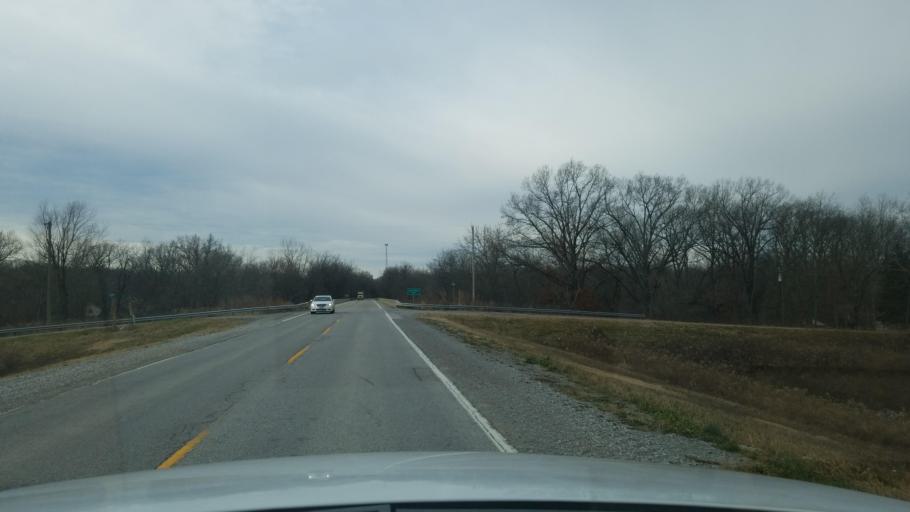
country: US
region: Illinois
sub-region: White County
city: Carmi
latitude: 37.9130
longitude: -88.1270
